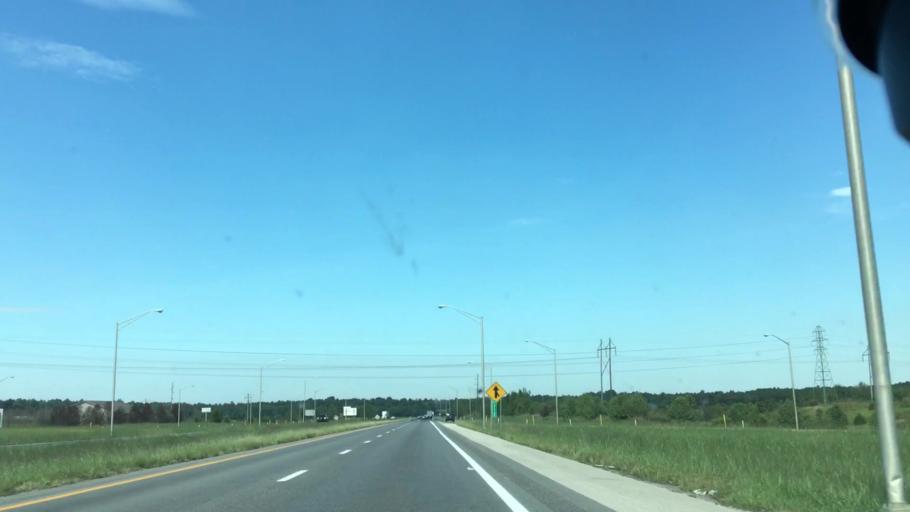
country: US
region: Kentucky
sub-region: Hopkins County
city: Madisonville
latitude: 37.2957
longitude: -87.4624
